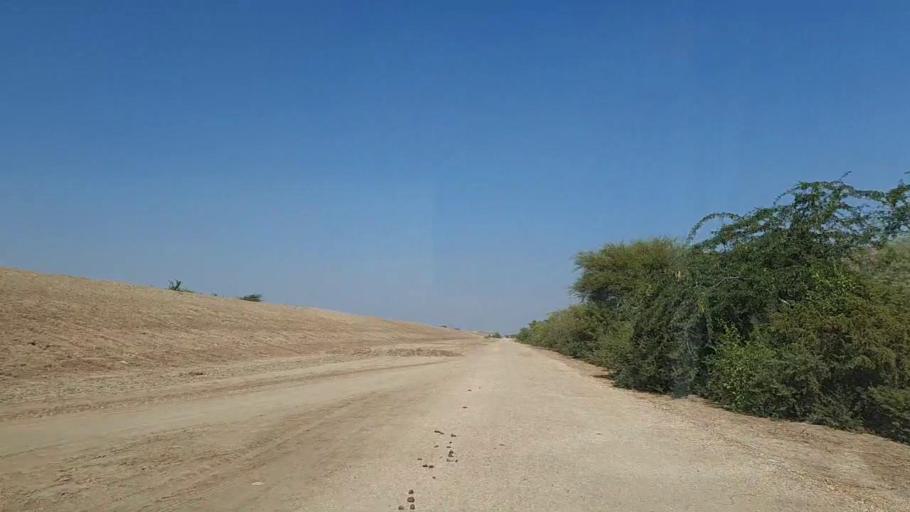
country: PK
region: Sindh
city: Chuhar Jamali
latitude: 24.4625
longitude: 68.0033
